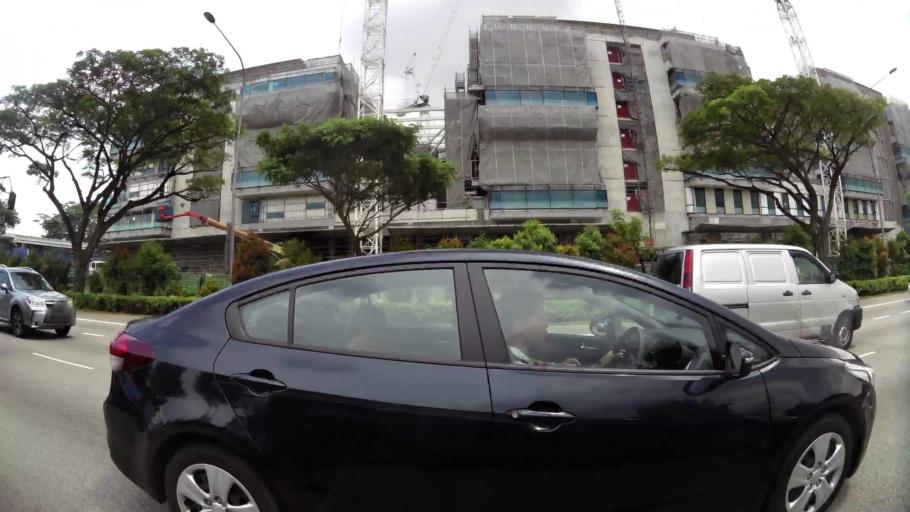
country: SG
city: Singapore
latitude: 1.3506
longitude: 103.8579
